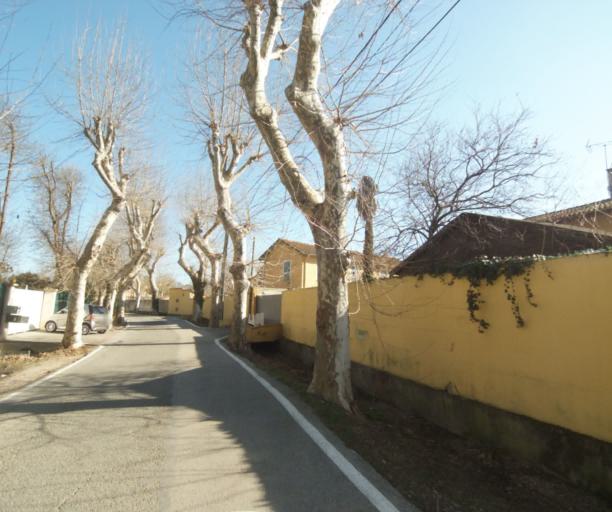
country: FR
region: Provence-Alpes-Cote d'Azur
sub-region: Departement des Alpes-Maritimes
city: Biot
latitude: 43.6119
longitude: 7.1214
